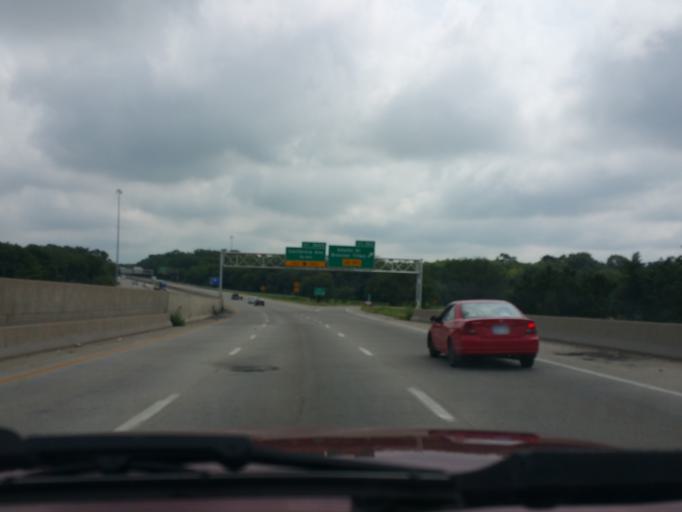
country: US
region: Kansas
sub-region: Shawnee County
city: Topeka
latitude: 39.0396
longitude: -95.6682
